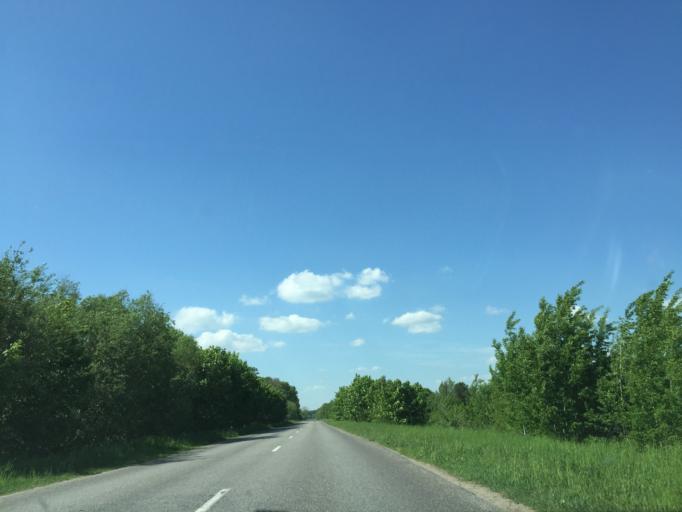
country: LV
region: Rundales
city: Pilsrundale
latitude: 56.5928
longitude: 23.9601
